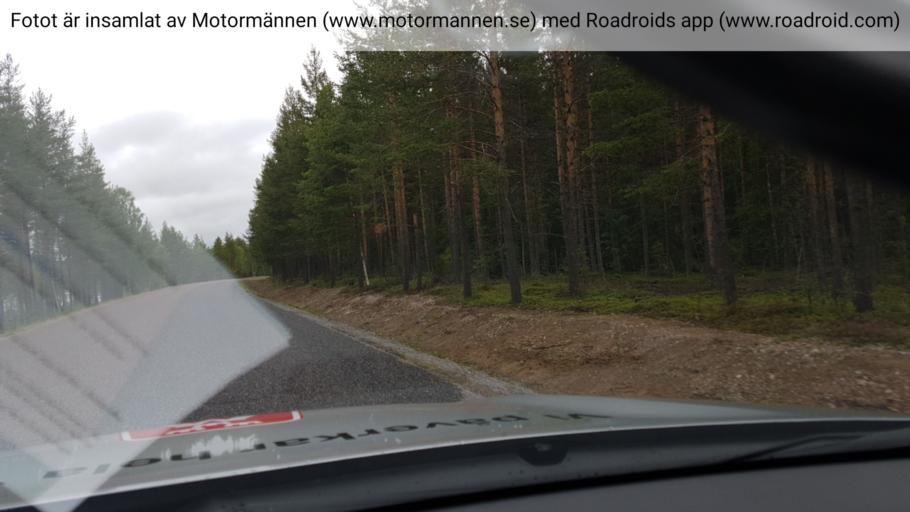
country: SE
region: Norrbotten
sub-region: Gallivare Kommun
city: Gaellivare
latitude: 66.5031
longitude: 20.5760
